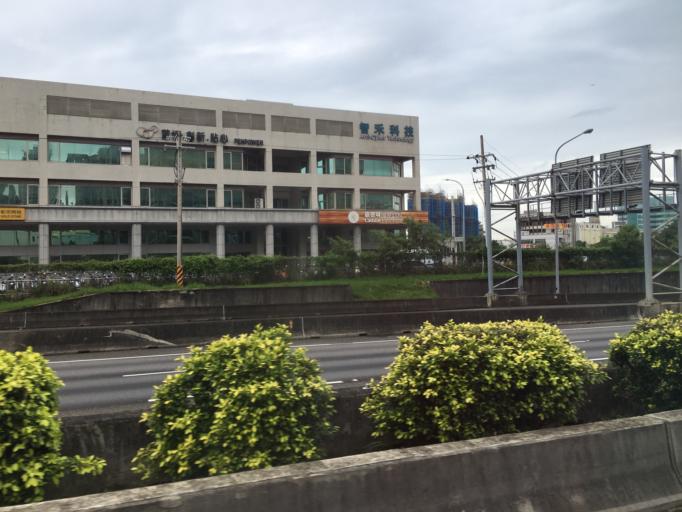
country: TW
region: Taiwan
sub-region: Hsinchu
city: Hsinchu
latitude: 24.7941
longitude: 121.0072
